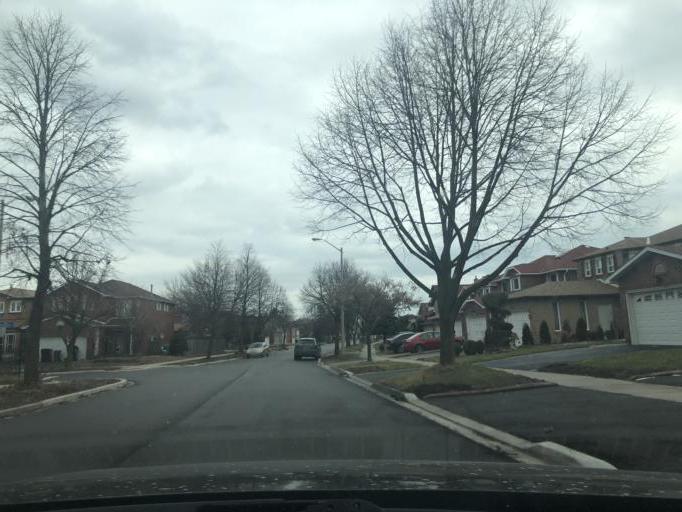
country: CA
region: Ontario
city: Scarborough
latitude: 43.7943
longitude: -79.1858
